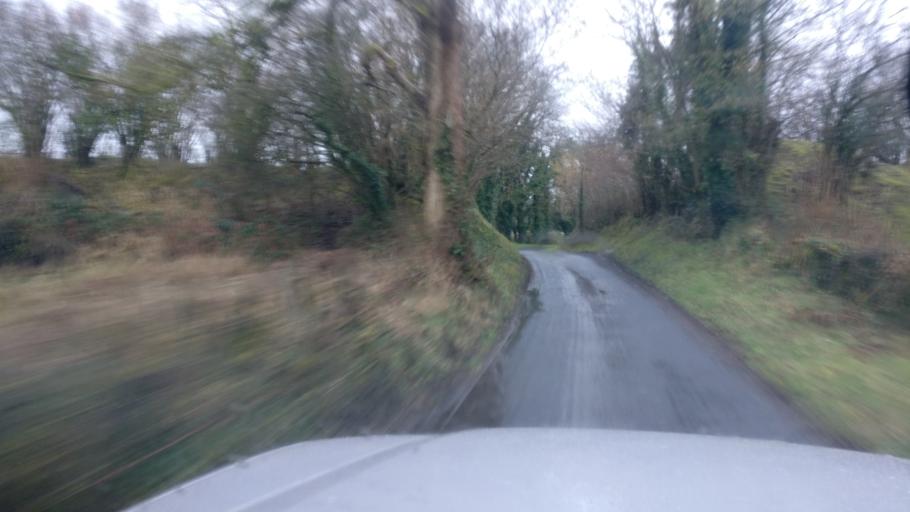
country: IE
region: Connaught
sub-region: County Galway
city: Ballinasloe
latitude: 53.2966
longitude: -8.2714
